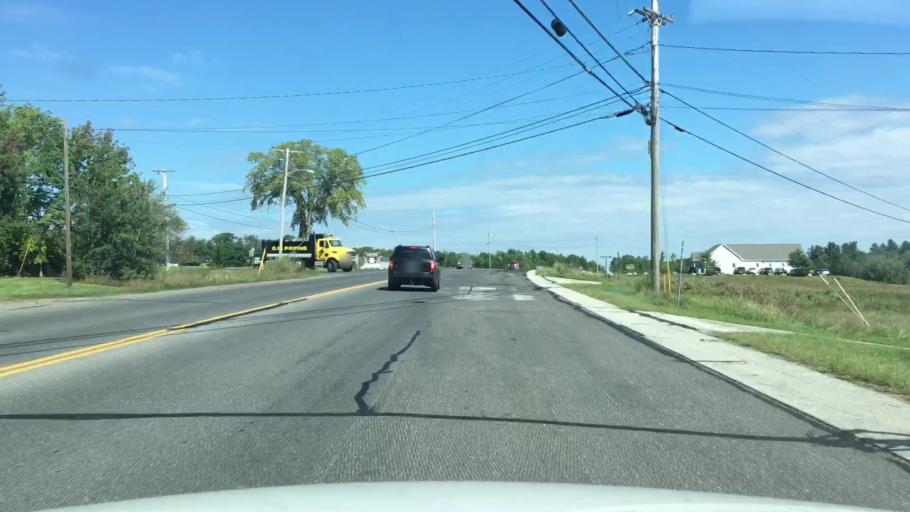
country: US
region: Maine
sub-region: Penobscot County
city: Newport
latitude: 44.8603
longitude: -69.2845
